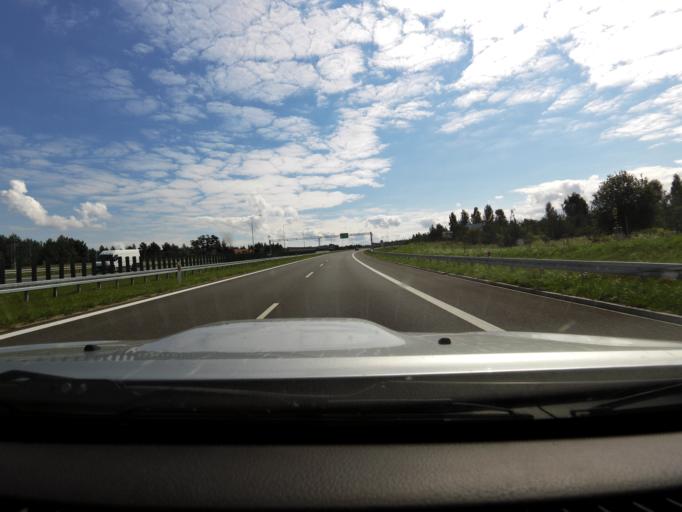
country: PL
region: Warmian-Masurian Voivodeship
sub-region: Powiat ostrodzki
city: Milomlyn
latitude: 53.7716
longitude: 19.8455
